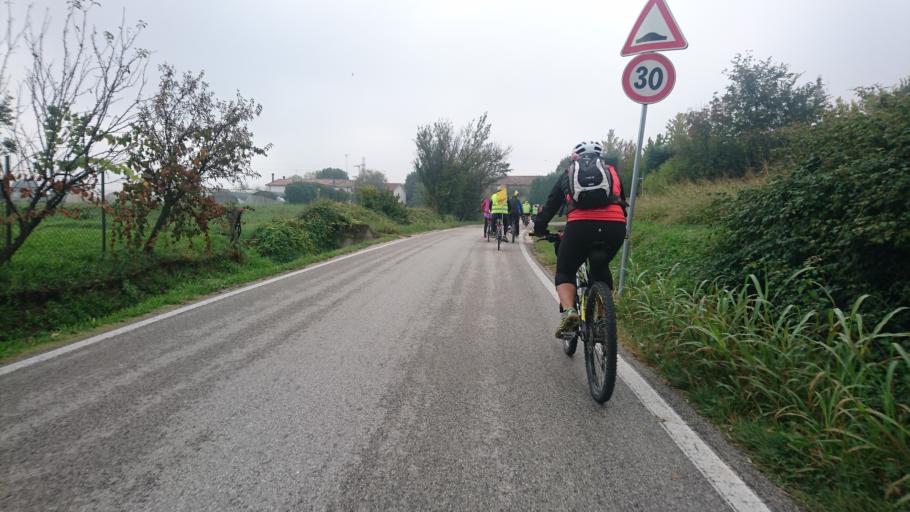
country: IT
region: Veneto
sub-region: Provincia di Padova
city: Monselice
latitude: 45.2308
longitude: 11.7659
